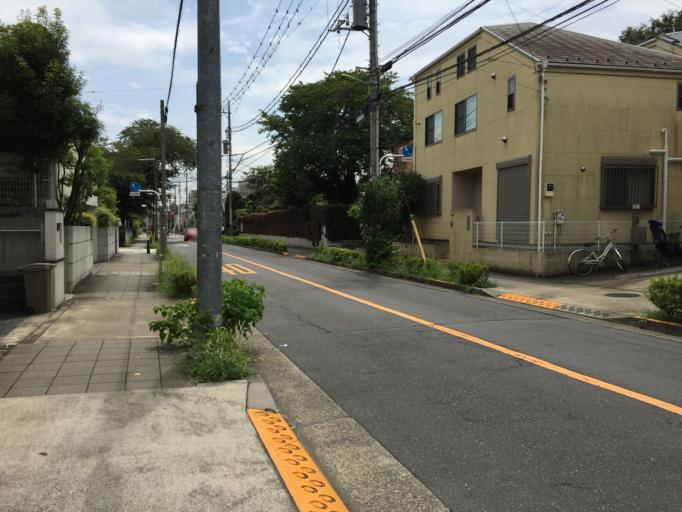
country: JP
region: Tokyo
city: Tokyo
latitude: 35.6596
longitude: 139.6378
